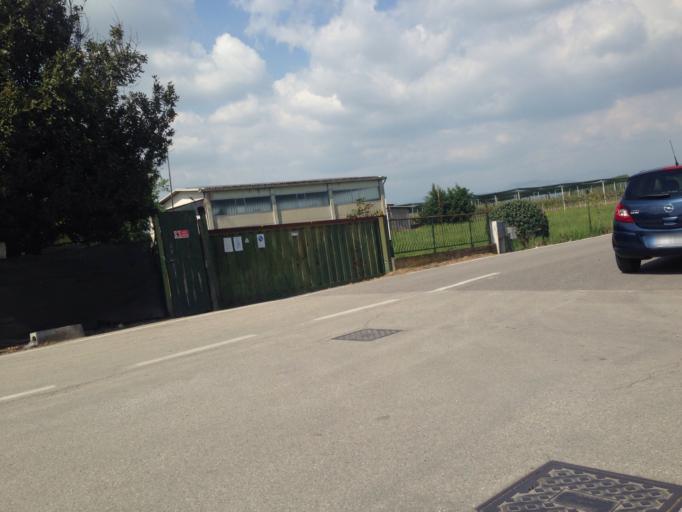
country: IT
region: Veneto
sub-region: Provincia di Verona
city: Zevio
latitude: 45.3716
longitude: 11.1077
